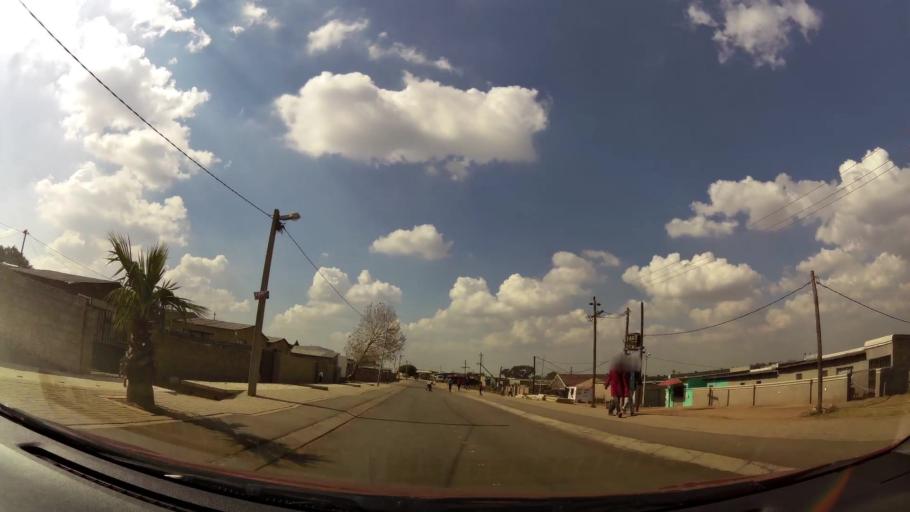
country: ZA
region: Gauteng
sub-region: City of Johannesburg Metropolitan Municipality
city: Roodepoort
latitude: -26.1934
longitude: 27.8742
